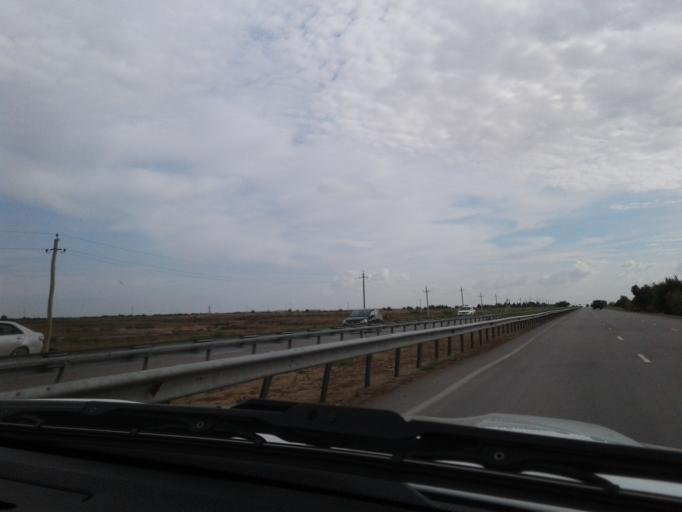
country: TM
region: Mary
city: Mary
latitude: 37.4846
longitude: 61.6939
